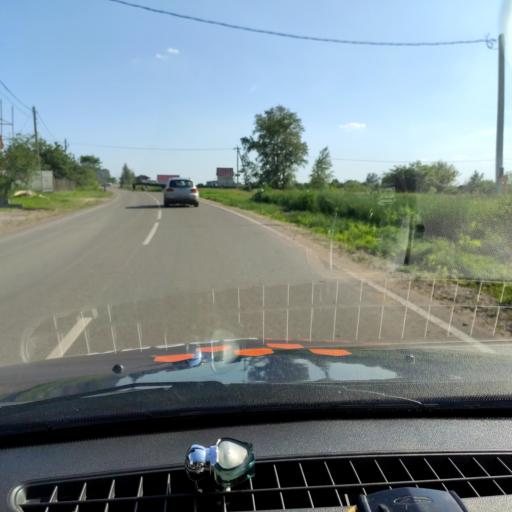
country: RU
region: Voronezj
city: Podgornoye
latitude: 51.8496
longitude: 39.1471
